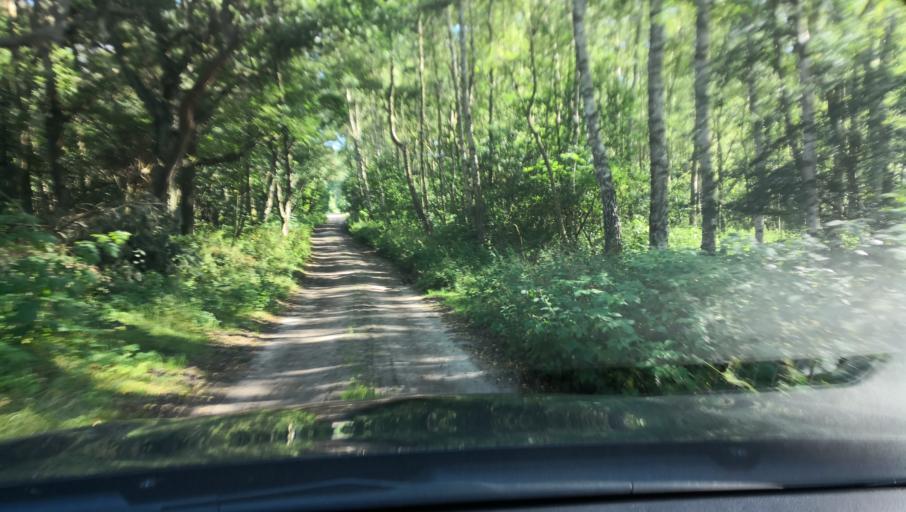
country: SE
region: Skane
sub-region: Kristianstads Kommun
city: Degeberga
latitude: 55.7979
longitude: 14.1954
